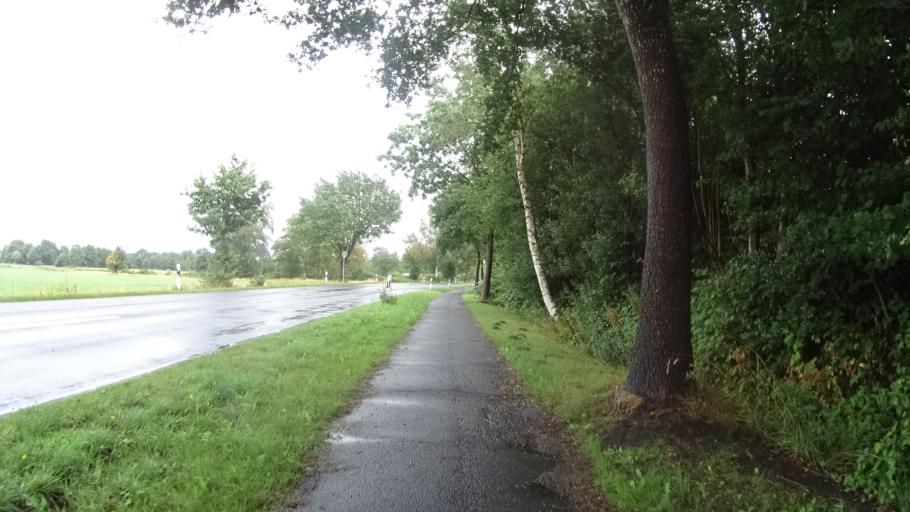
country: DE
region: Lower Saxony
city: Firrel
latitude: 53.3317
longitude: 7.6568
